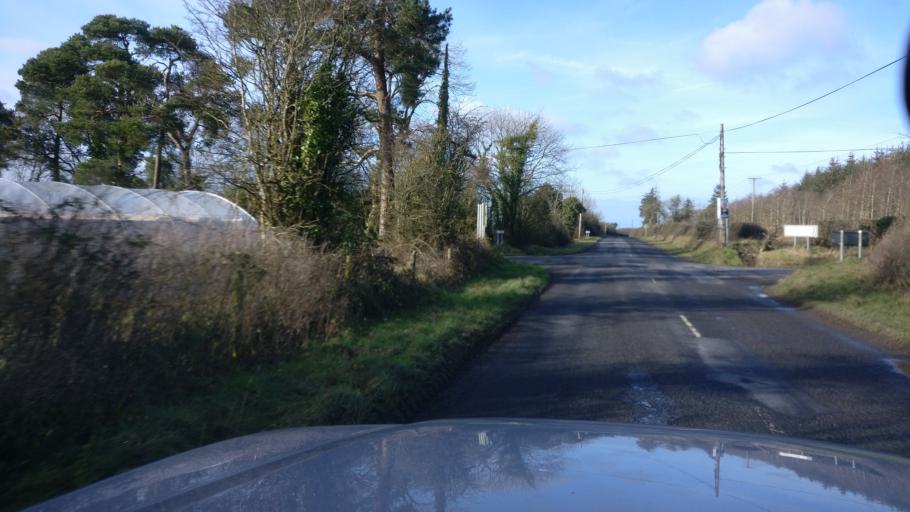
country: IE
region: Leinster
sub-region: Laois
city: Stradbally
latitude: 52.9272
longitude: -7.1959
